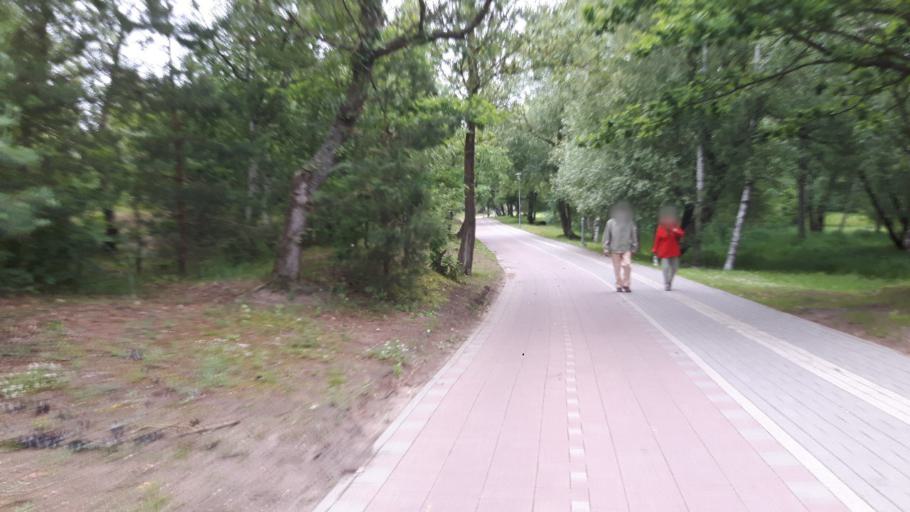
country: LV
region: Liepaja
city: Liepaja
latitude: 56.4976
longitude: 20.9960
